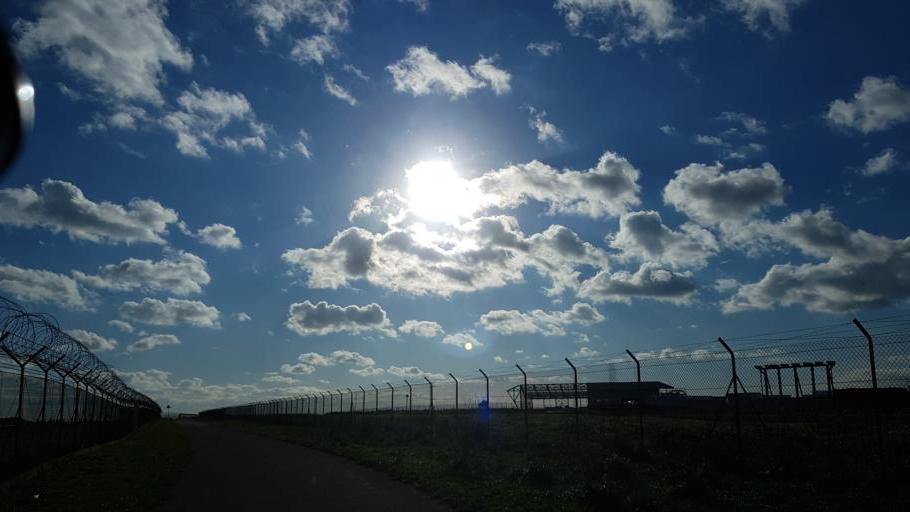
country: IT
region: Apulia
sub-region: Provincia di Brindisi
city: Materdomini
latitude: 40.6751
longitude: 17.9225
